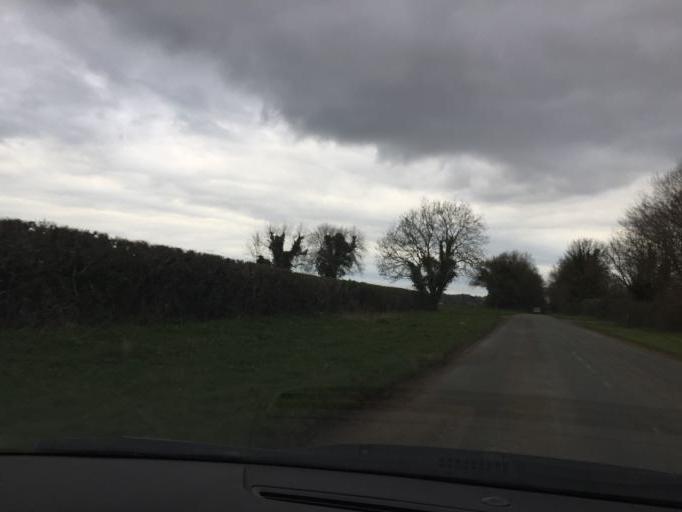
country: GB
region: England
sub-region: Oxfordshire
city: Chipping Norton
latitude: 51.9607
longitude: -1.5343
